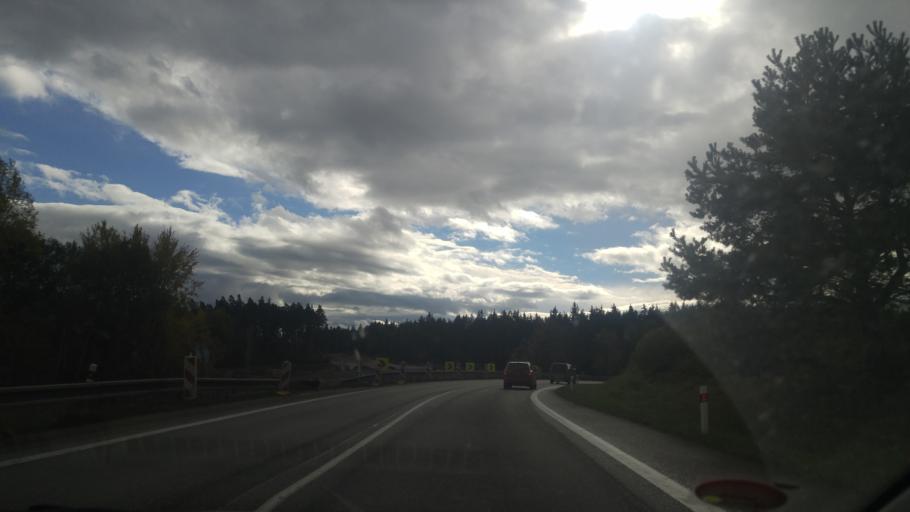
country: CZ
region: Jihocesky
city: Borek
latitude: 49.0304
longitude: 14.5087
